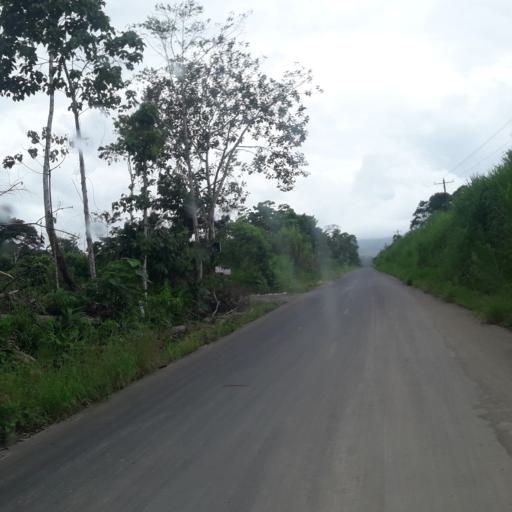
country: EC
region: Napo
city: Tena
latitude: -1.0496
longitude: -77.6636
